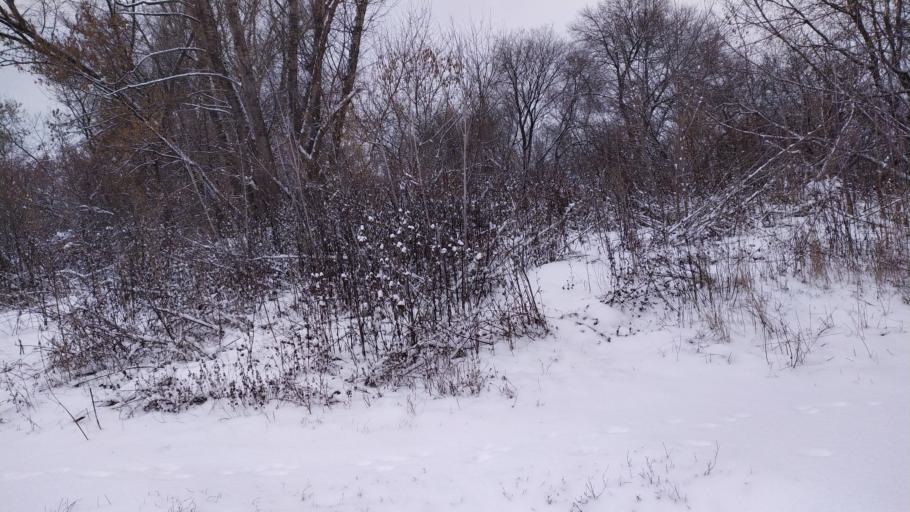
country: RU
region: Kursk
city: Kursk
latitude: 51.6562
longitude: 36.1471
